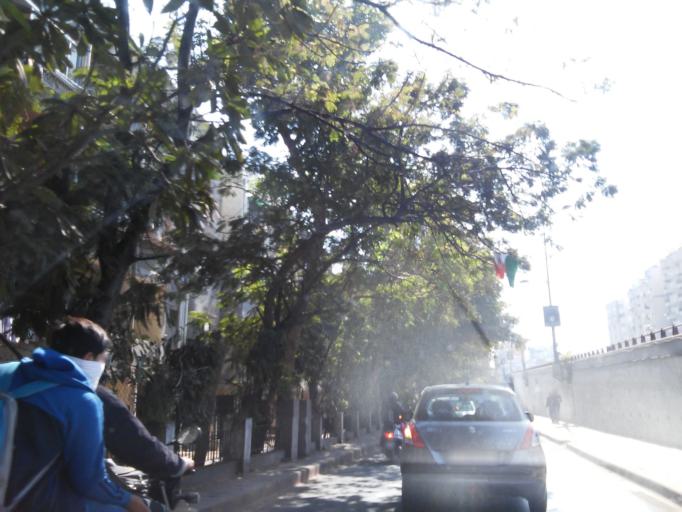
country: IN
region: Gujarat
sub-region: Ahmadabad
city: Sarkhej
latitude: 23.0271
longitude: 72.5313
